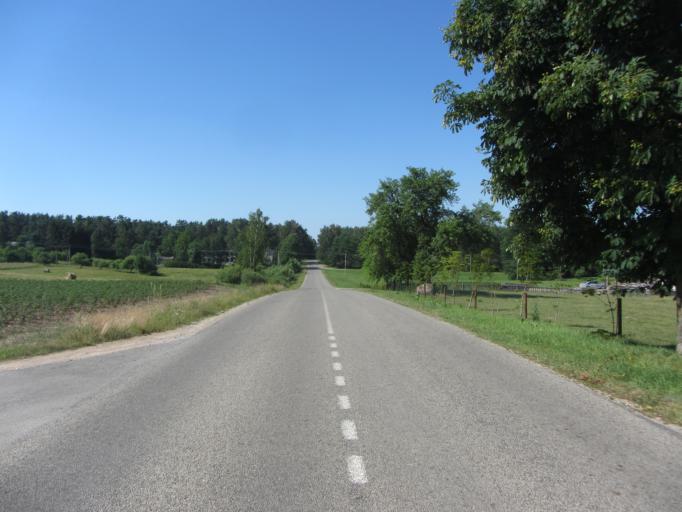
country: LT
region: Alytaus apskritis
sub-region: Alytus
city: Alytus
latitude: 54.3377
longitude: 24.1105
